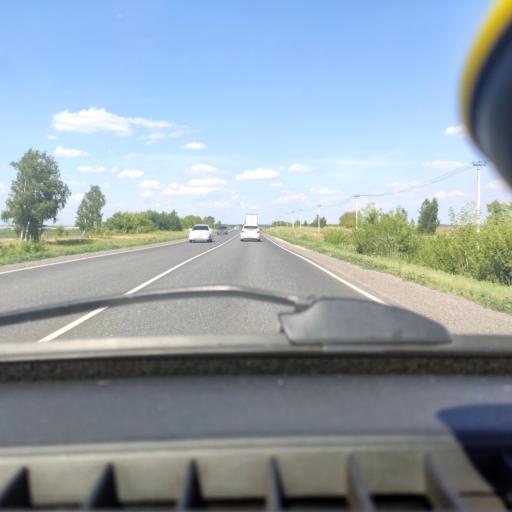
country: RU
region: Samara
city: Povolzhskiy
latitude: 53.6893
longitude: 49.7309
